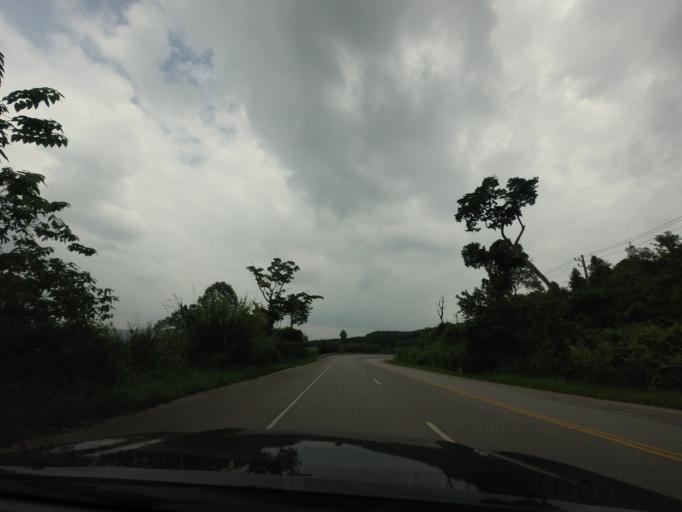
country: TH
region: Loei
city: Dan Sai
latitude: 17.2834
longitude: 101.2416
